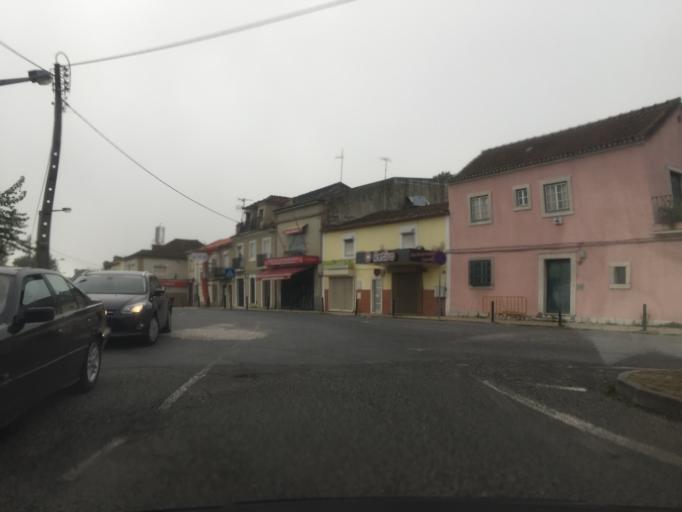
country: PT
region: Lisbon
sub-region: Loures
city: Camarate
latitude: 38.7852
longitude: -9.1429
